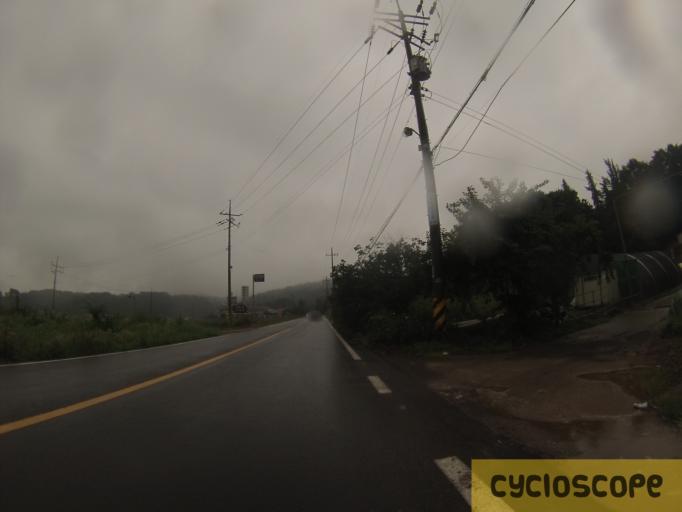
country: KR
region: Jeollabuk-do
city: Kunsan
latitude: 36.0715
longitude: 126.6530
